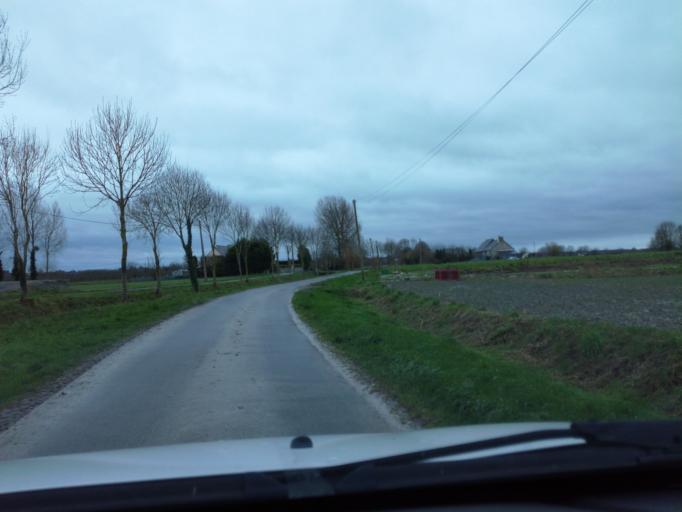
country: FR
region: Brittany
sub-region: Departement d'Ille-et-Vilaine
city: Dol-de-Bretagne
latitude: 48.5636
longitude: -1.7322
